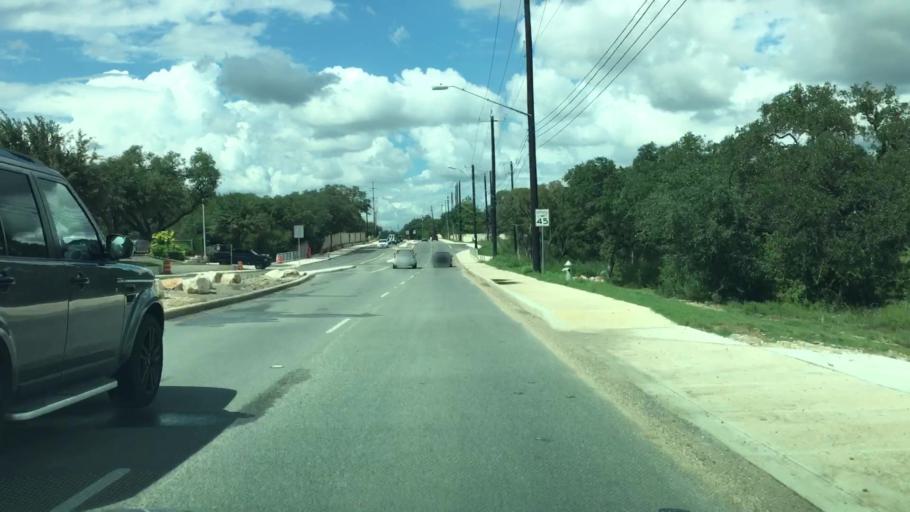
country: US
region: Texas
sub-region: Bexar County
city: Hollywood Park
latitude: 29.6040
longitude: -98.4433
